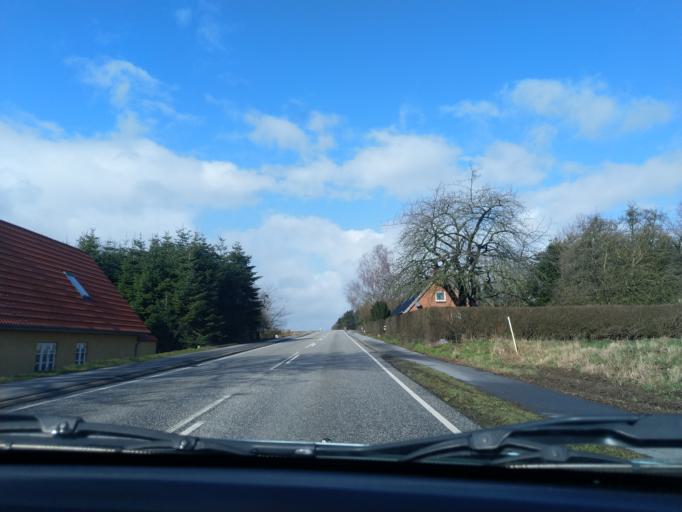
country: DK
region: Zealand
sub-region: Naestved Kommune
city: Naestved
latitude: 55.3072
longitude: 11.6877
